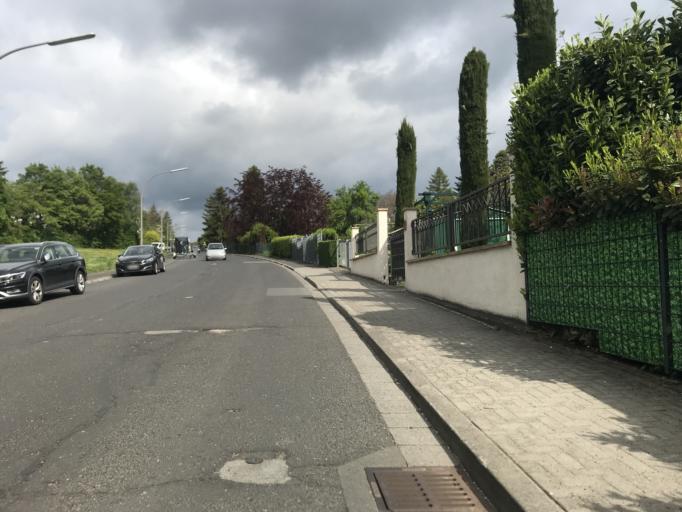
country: DE
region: Hesse
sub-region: Regierungsbezirk Darmstadt
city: Walluf
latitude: 50.0589
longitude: 8.1910
